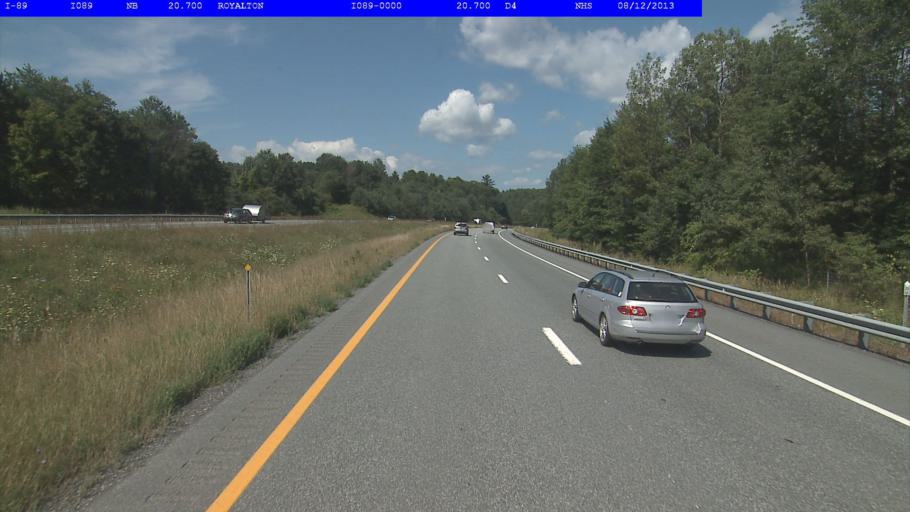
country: US
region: Vermont
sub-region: Orange County
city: Randolph
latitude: 43.8116
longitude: -72.5586
